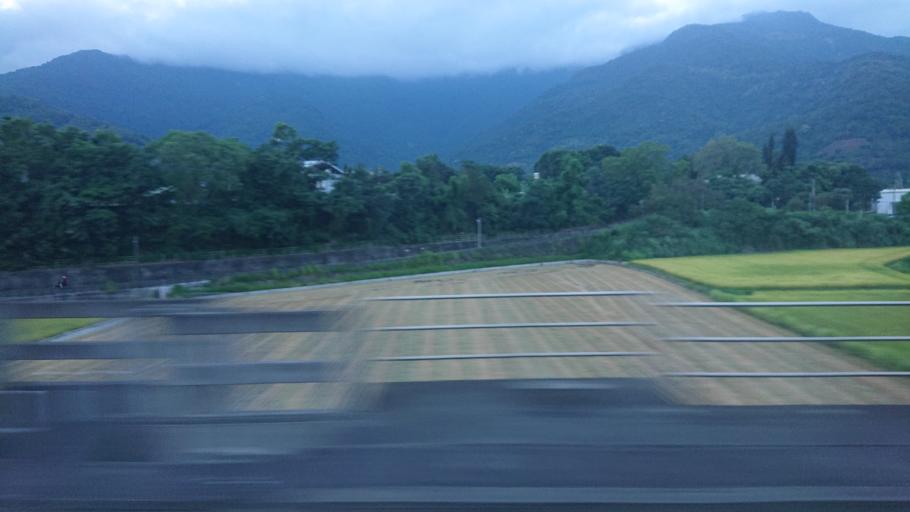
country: TW
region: Taiwan
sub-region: Taitung
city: Taitung
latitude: 23.0396
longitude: 121.1625
